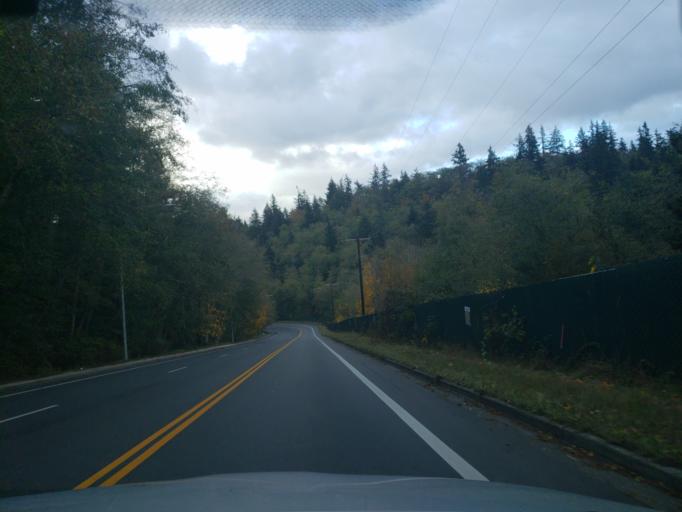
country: US
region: Washington
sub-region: Snohomish County
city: Mukilteo
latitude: 47.9388
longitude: -122.2789
